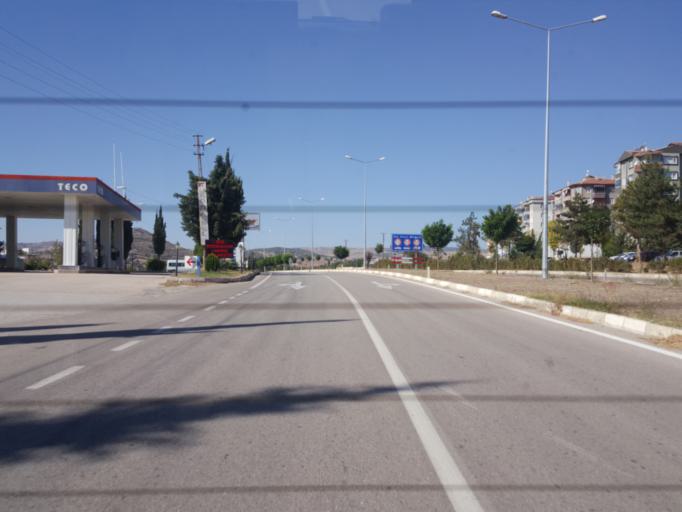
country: TR
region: Tokat
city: Zile
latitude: 40.2920
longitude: 35.8737
